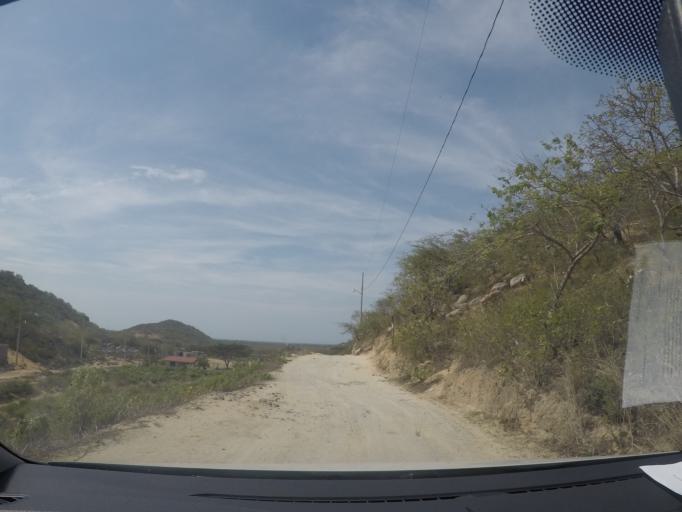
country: MX
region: Oaxaca
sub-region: Salina Cruz
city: Salina Cruz
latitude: 16.2164
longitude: -95.1255
